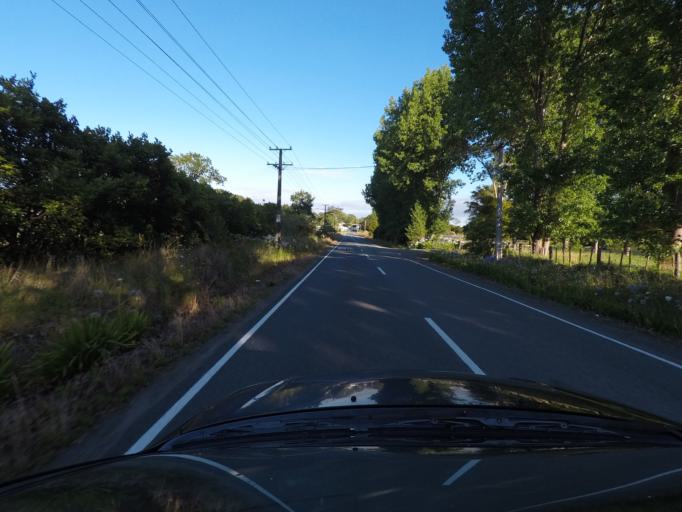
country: NZ
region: Northland
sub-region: Whangarei
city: Whangarei
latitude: -35.6431
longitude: 174.2999
